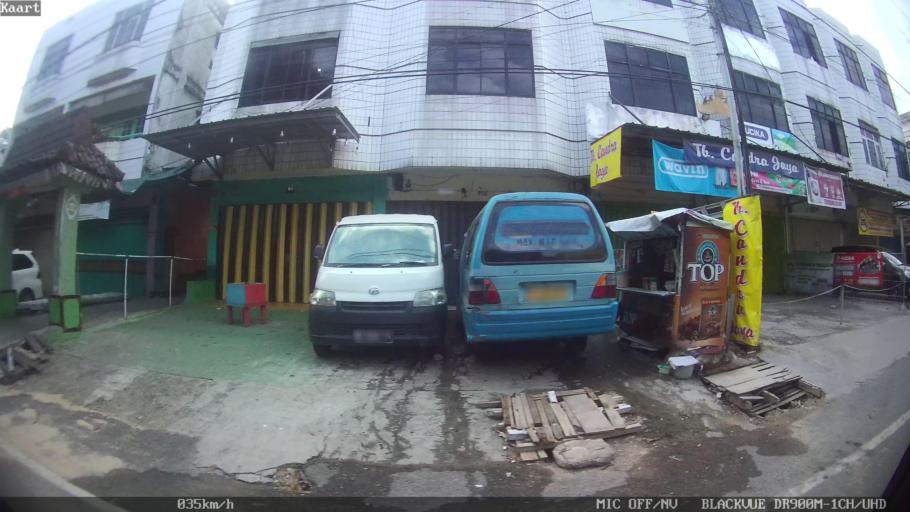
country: ID
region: Lampung
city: Bandarlampung
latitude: -5.4107
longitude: 105.2615
